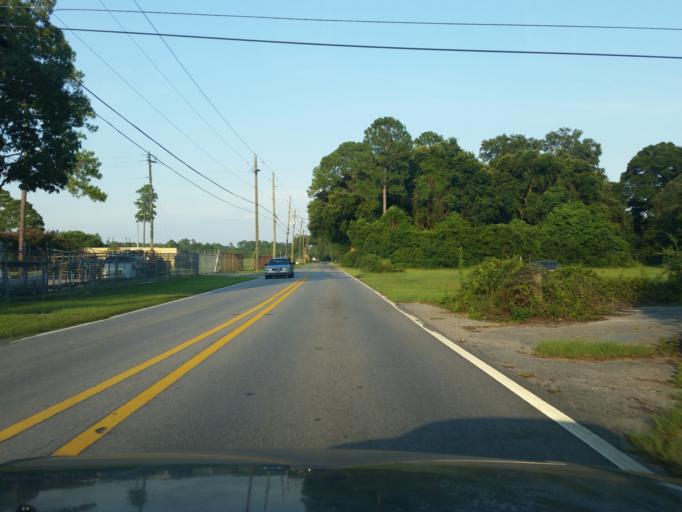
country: US
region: Florida
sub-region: Escambia County
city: Ferry Pass
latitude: 30.5172
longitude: -87.2002
